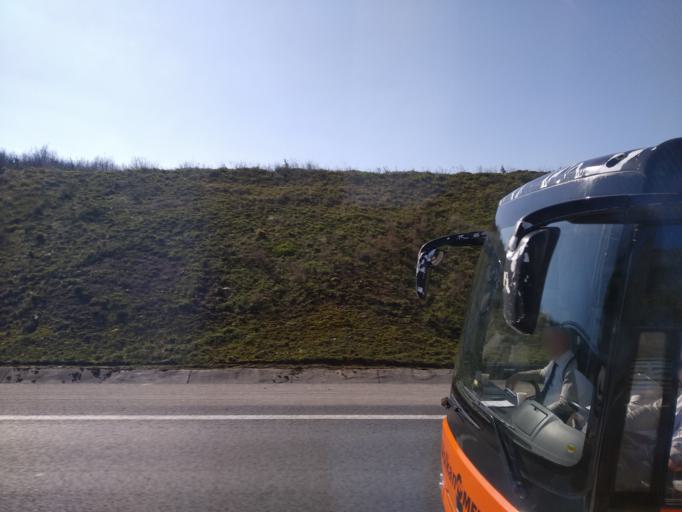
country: TR
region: Istanbul
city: Mahmut Sevket Pasa
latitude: 41.1747
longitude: 29.2421
